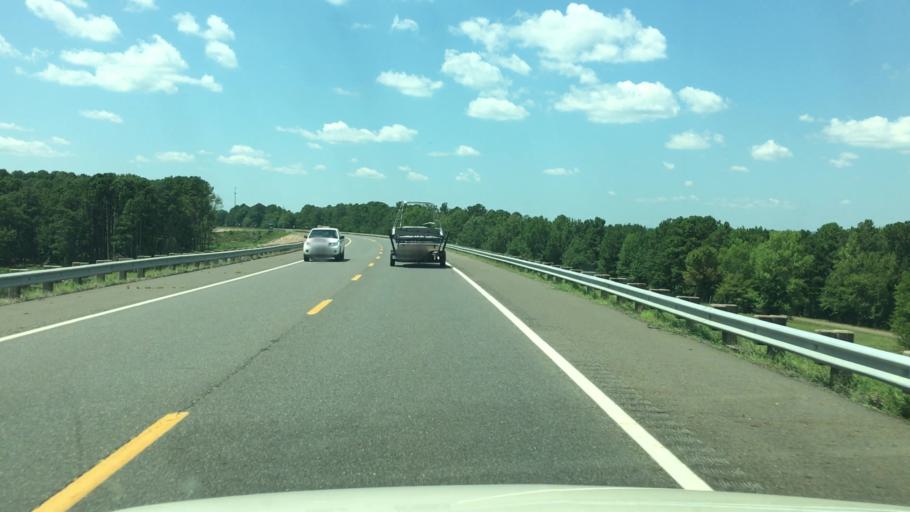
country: US
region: Arkansas
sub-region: Clark County
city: Arkadelphia
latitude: 34.2442
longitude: -93.1074
